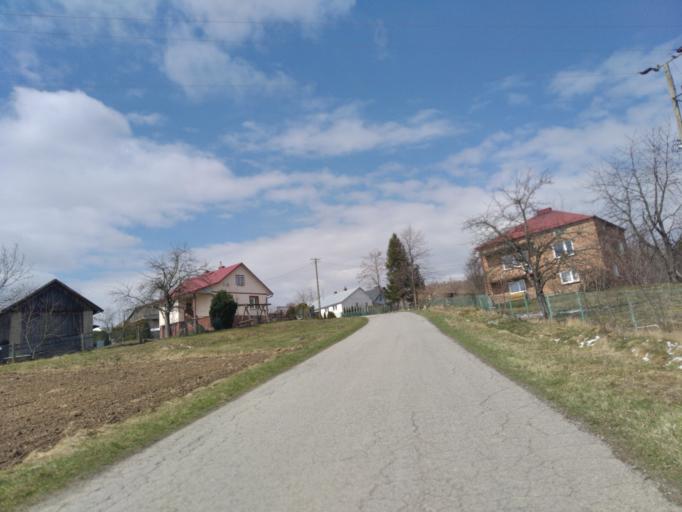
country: PL
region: Subcarpathian Voivodeship
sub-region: Powiat ropczycko-sedziszowski
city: Ropczyce
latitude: 50.0121
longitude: 21.5809
